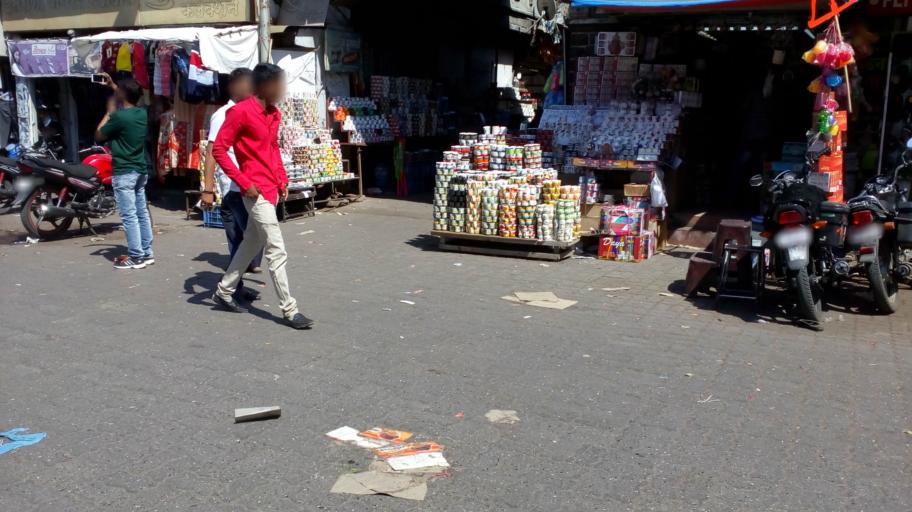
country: IN
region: Maharashtra
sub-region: Nashik Division
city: Nashik
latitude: 20.0018
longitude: 73.7888
